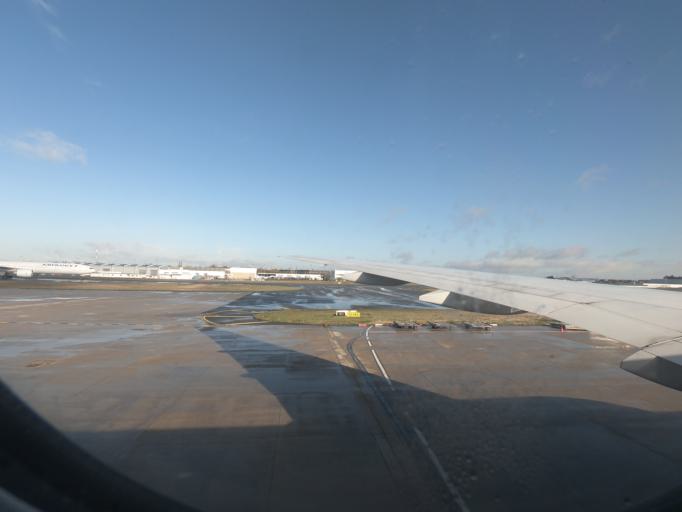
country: FR
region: Ile-de-France
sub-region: Departement de Seine-et-Marne
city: Mitry-Mory
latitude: 49.0077
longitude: 2.5888
